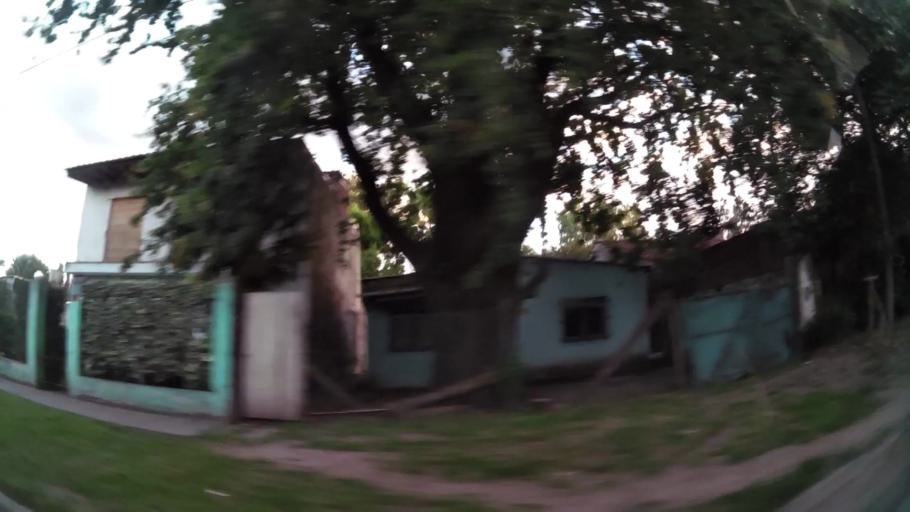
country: AR
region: Buenos Aires
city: Santa Catalina - Dique Lujan
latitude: -34.4906
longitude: -58.7562
